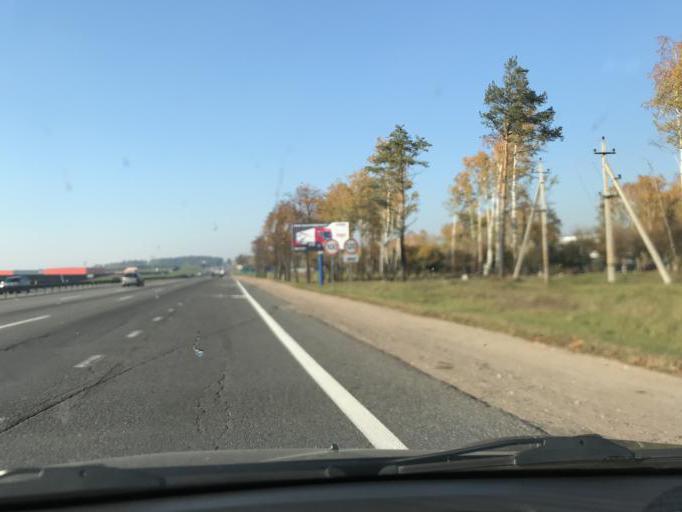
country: BY
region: Minsk
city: Pryvol'ny
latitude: 53.8071
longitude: 27.7892
